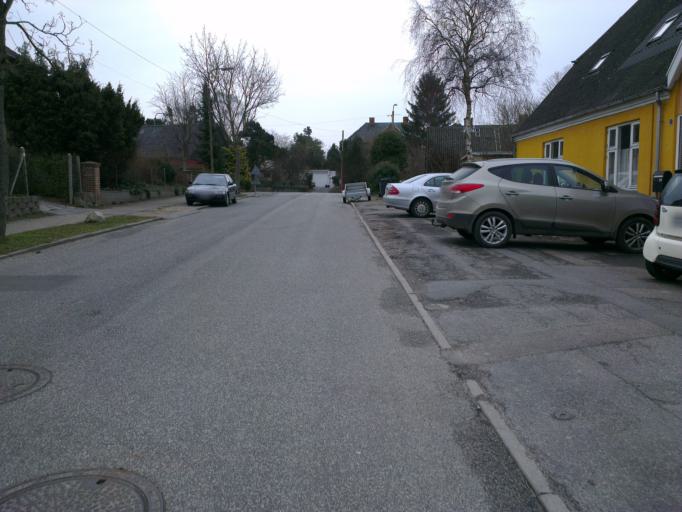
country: DK
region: Capital Region
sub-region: Frederikssund Kommune
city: Skibby
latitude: 55.7467
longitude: 11.9544
